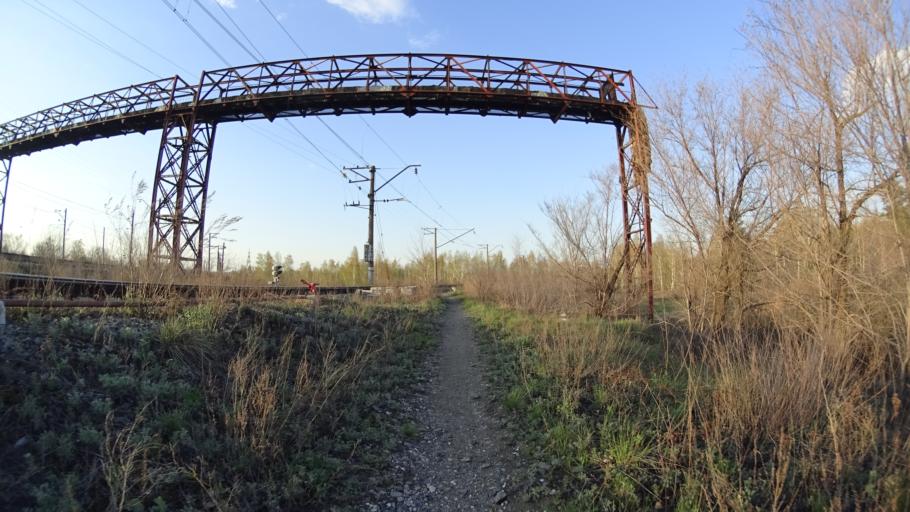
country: RU
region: Chelyabinsk
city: Troitsk
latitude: 54.0577
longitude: 61.6141
